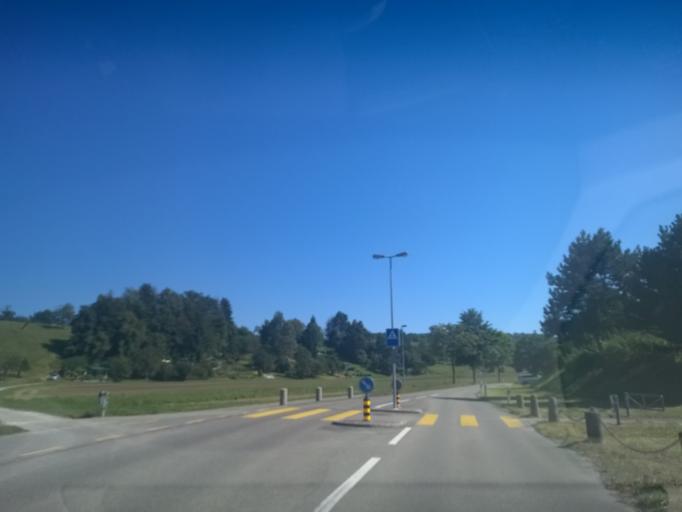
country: CH
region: Zurich
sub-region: Bezirk Buelach
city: Kloten / Geissberg
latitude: 47.4574
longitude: 8.5875
